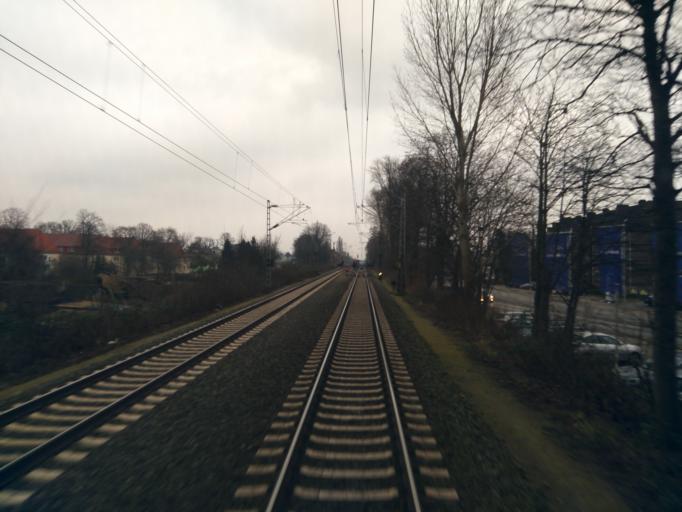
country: DE
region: Bremen
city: Bremen
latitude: 53.0649
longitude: 8.8807
